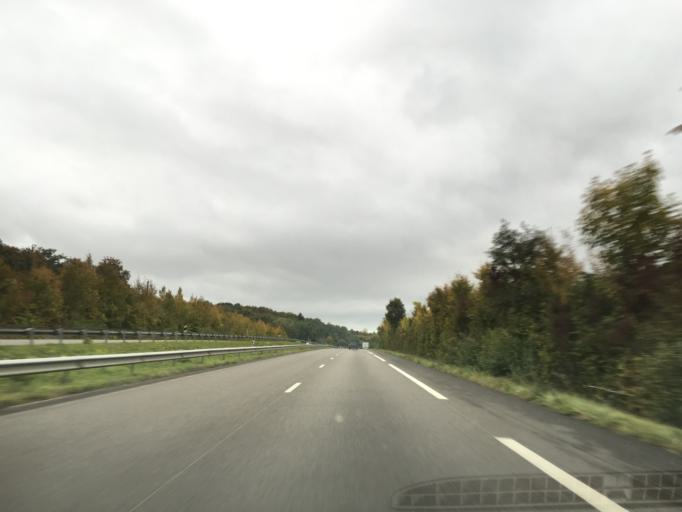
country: FR
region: Lorraine
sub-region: Departement de la Meuse
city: Vacon
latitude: 48.6892
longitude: 5.5568
